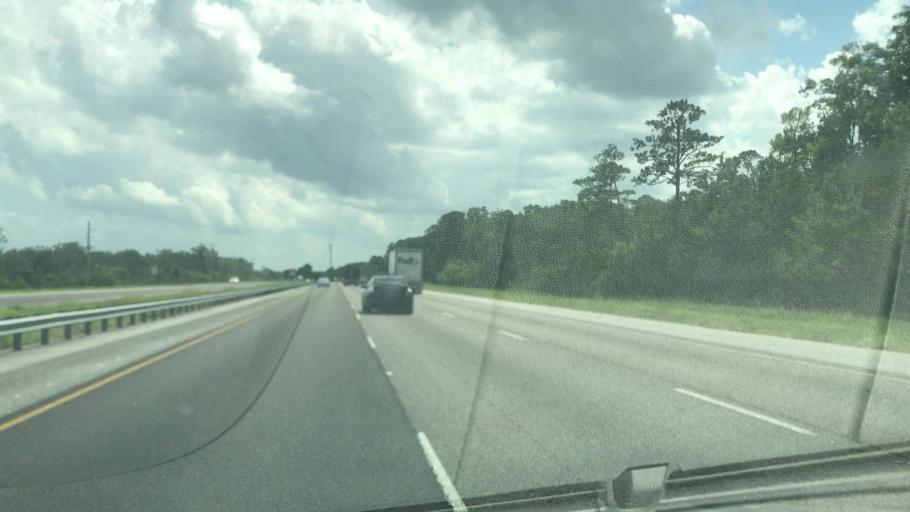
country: US
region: Georgia
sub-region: Liberty County
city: Midway
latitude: 31.8031
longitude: -81.3702
